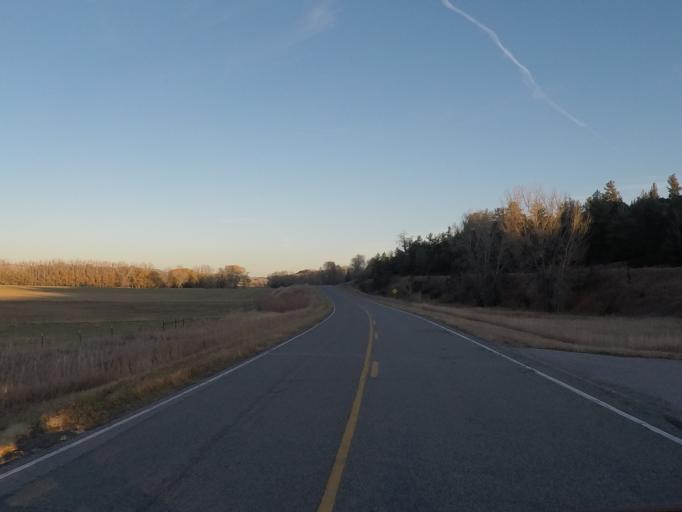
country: US
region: Montana
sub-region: Sweet Grass County
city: Big Timber
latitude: 45.7858
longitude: -109.8473
